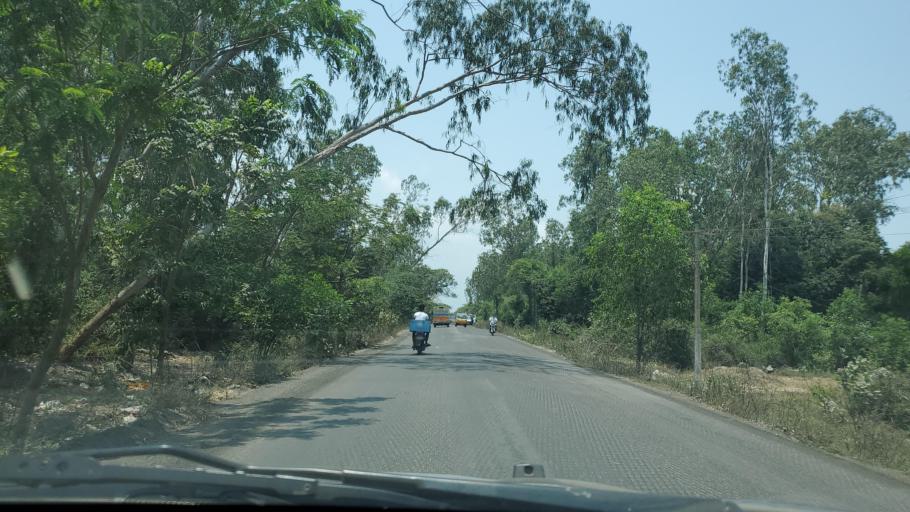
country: IN
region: Tamil Nadu
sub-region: Kancheepuram
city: Vengavasal
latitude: 12.8691
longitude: 80.1753
